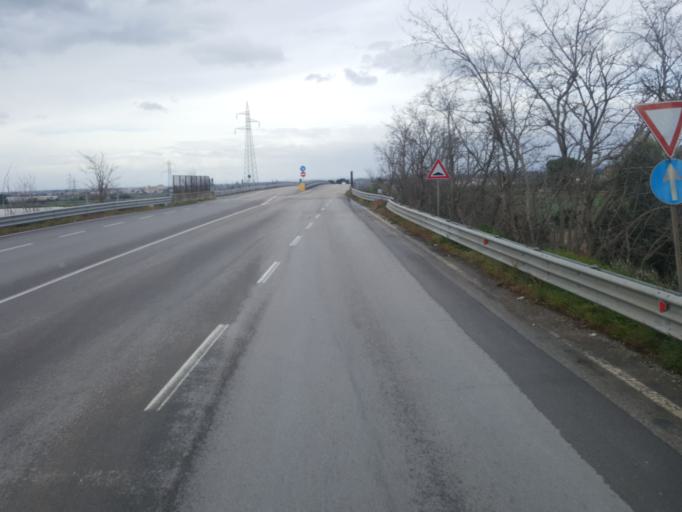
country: IT
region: Apulia
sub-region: Provincia di Taranto
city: Palagiano
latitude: 40.6008
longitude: 17.0699
